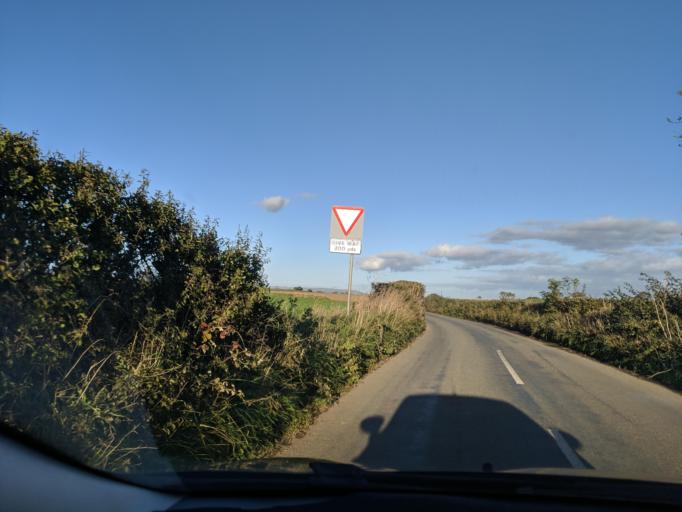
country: GB
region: England
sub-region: Plymouth
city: Plymstock
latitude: 50.3361
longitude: -4.0989
